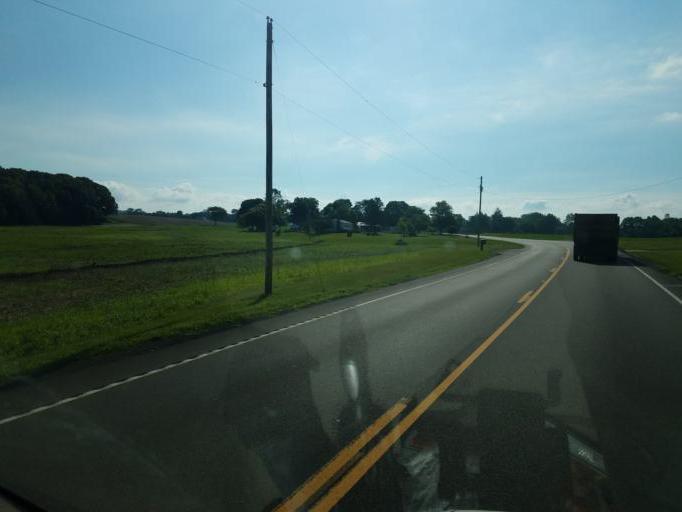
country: US
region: Ohio
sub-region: Knox County
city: Fredericktown
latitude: 40.4628
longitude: -82.6360
